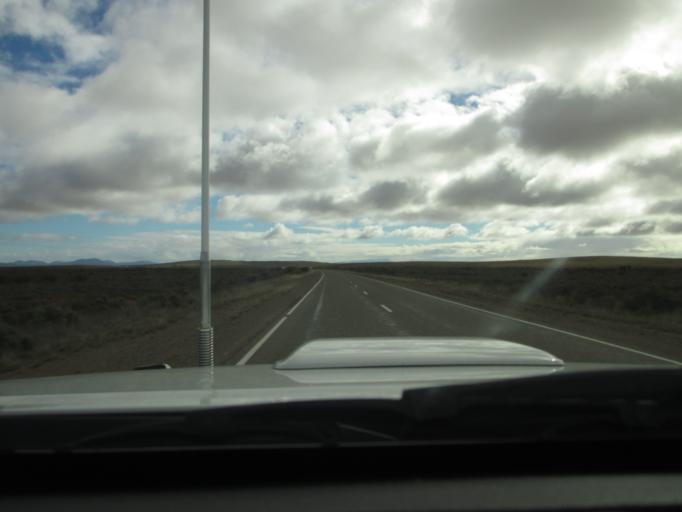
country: AU
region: South Australia
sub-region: Flinders Ranges
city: Quorn
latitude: -32.1164
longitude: 138.5054
